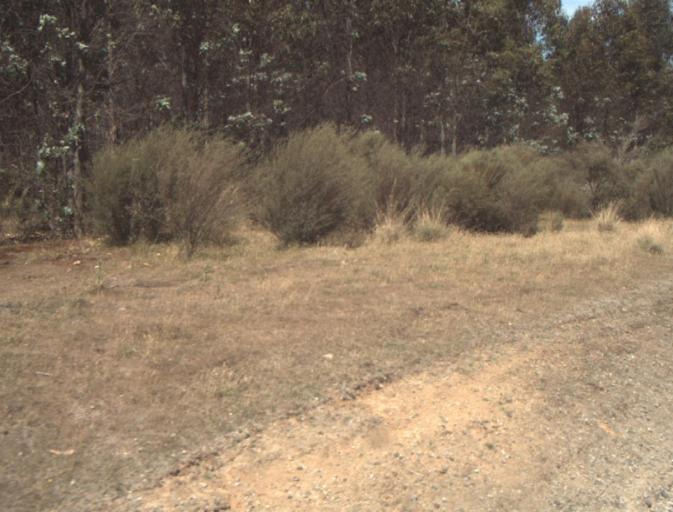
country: AU
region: Tasmania
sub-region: Dorset
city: Scottsdale
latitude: -41.3116
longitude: 147.4659
